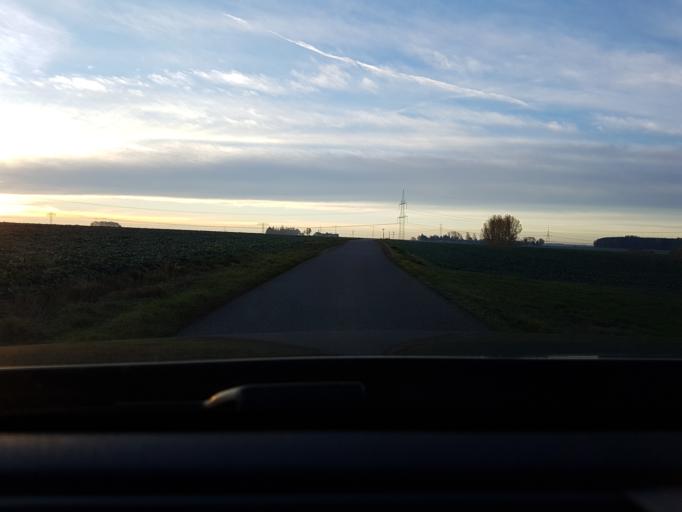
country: DE
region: Saxony
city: Altmittweida
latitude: 50.9632
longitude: 12.9671
